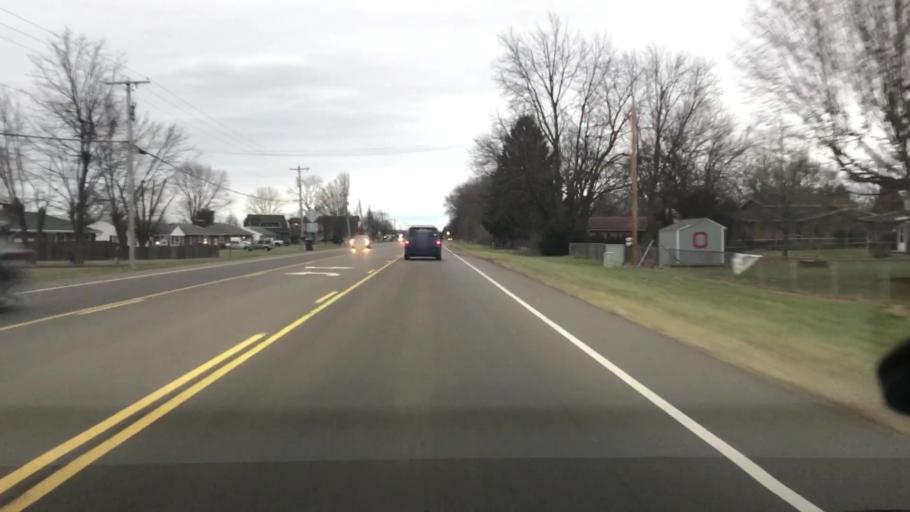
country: US
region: Ohio
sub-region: Clark County
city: Holiday Valley
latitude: 39.8571
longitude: -83.9715
